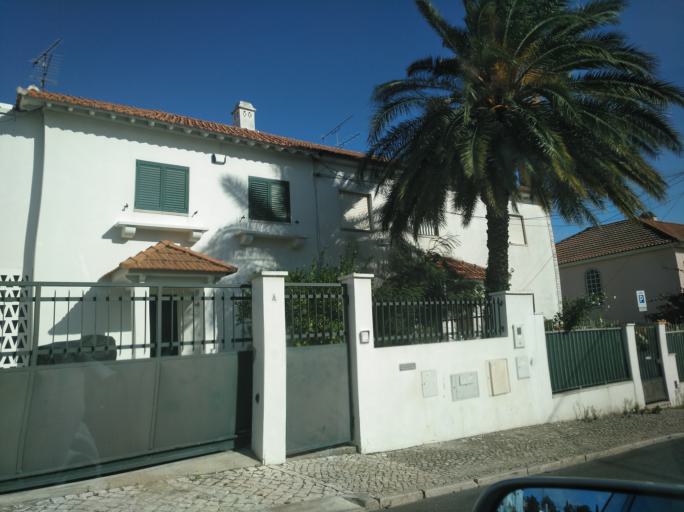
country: PT
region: Lisbon
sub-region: Loures
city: Moscavide
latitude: 38.7710
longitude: -9.1171
